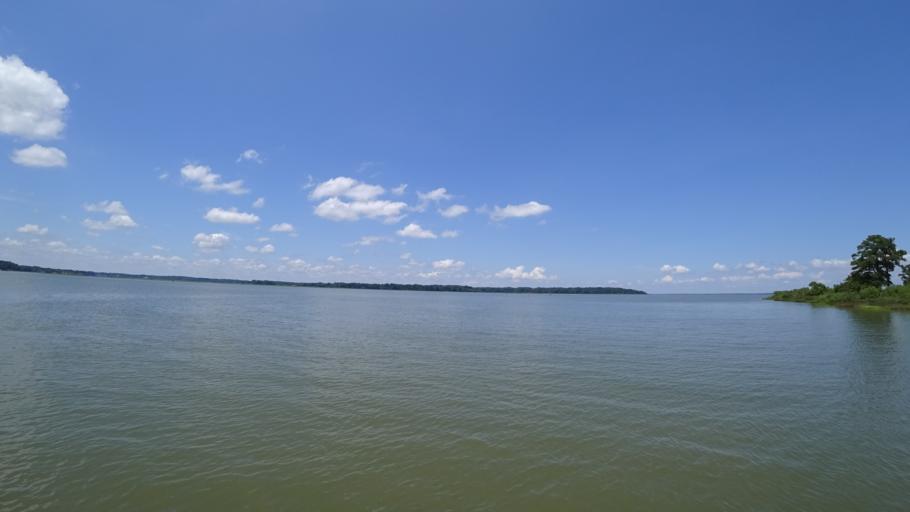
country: US
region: Virginia
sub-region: Isle of Wight County
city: Carrollton
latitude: 36.9992
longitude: -76.5702
